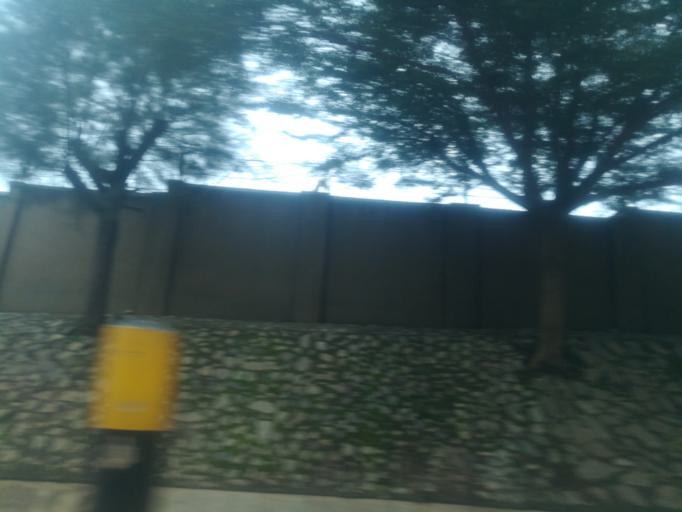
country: NG
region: Oyo
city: Ibadan
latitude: 7.3957
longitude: 3.9659
